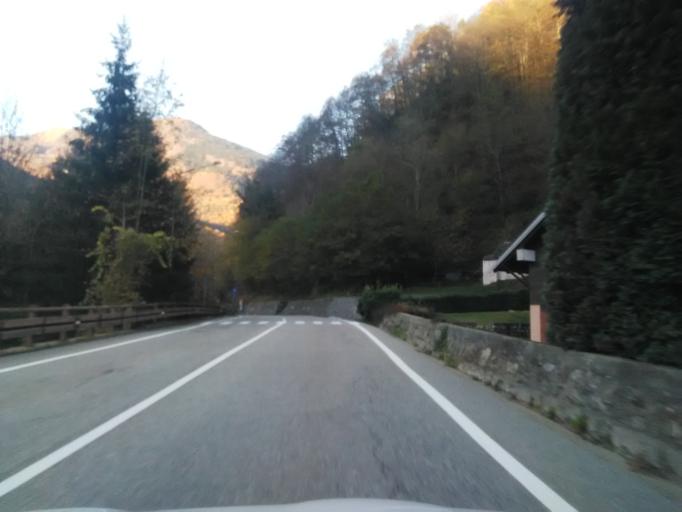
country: IT
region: Piedmont
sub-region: Provincia di Vercelli
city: Scopello
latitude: 45.7719
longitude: 8.0907
